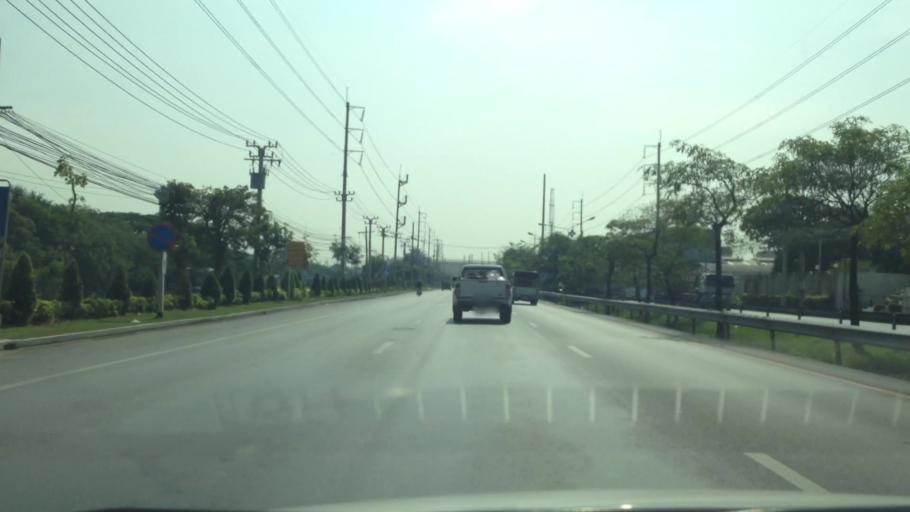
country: TH
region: Samut Prakan
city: Samut Prakan
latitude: 13.5281
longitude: 100.6365
